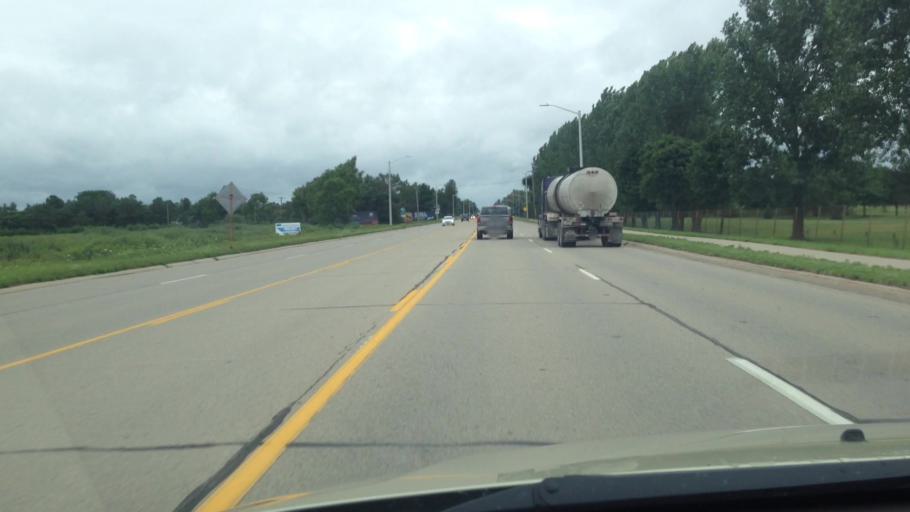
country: US
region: Michigan
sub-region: Delta County
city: Escanaba
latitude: 45.7263
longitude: -87.0800
